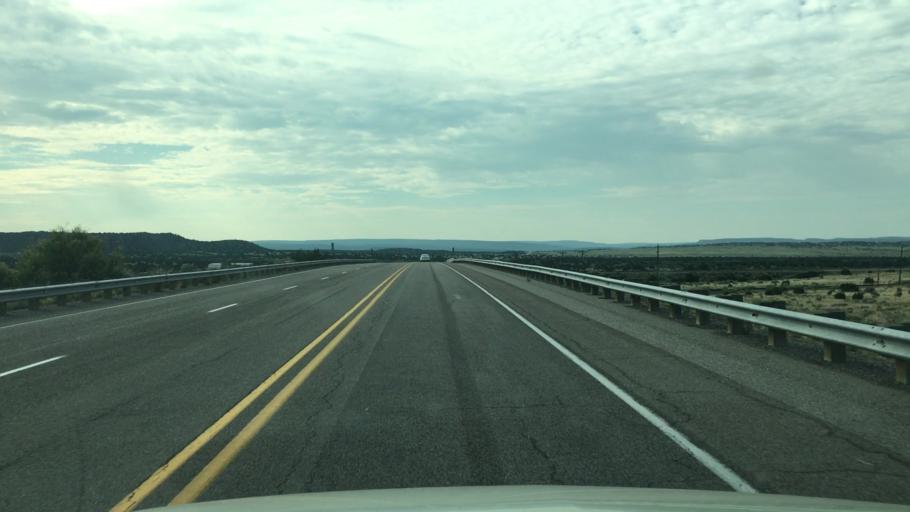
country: US
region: New Mexico
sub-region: Santa Fe County
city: Eldorado at Santa Fe
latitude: 35.4669
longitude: -105.9012
